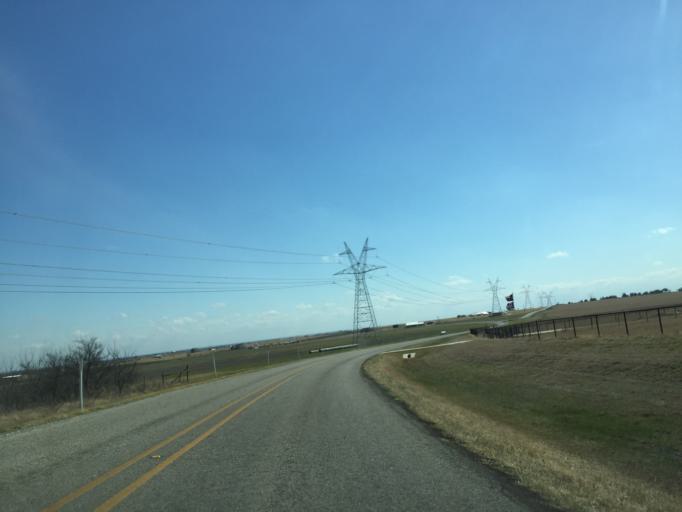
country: US
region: Texas
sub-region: Williamson County
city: Granger
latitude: 30.7577
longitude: -97.5250
